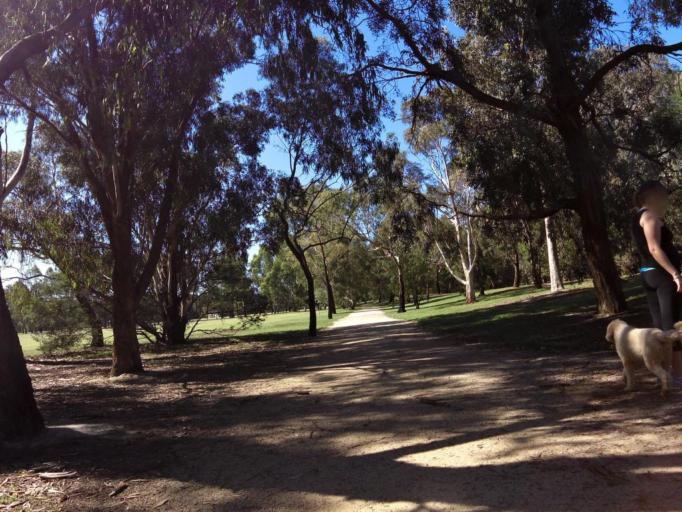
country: AU
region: Victoria
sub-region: Boroondara
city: Kew East
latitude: -37.7901
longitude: 145.0596
